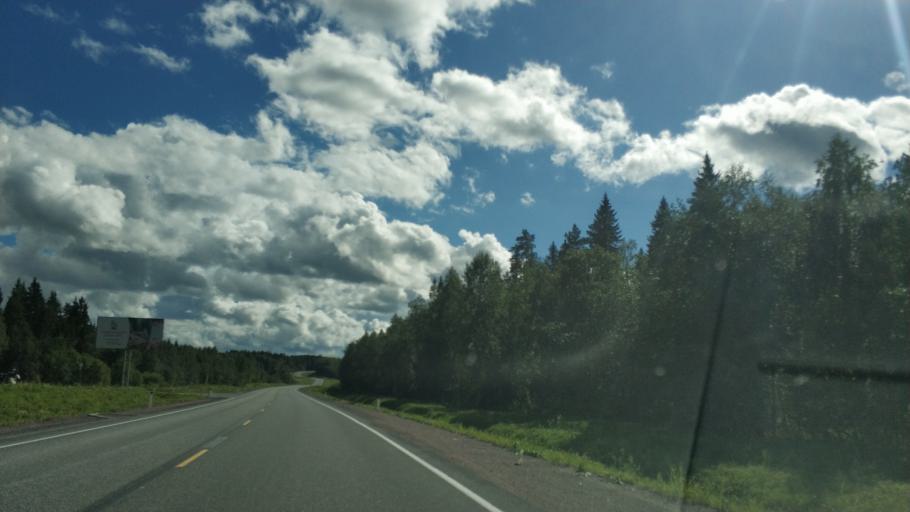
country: RU
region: Republic of Karelia
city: Ruskeala
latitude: 61.8777
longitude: 30.6452
